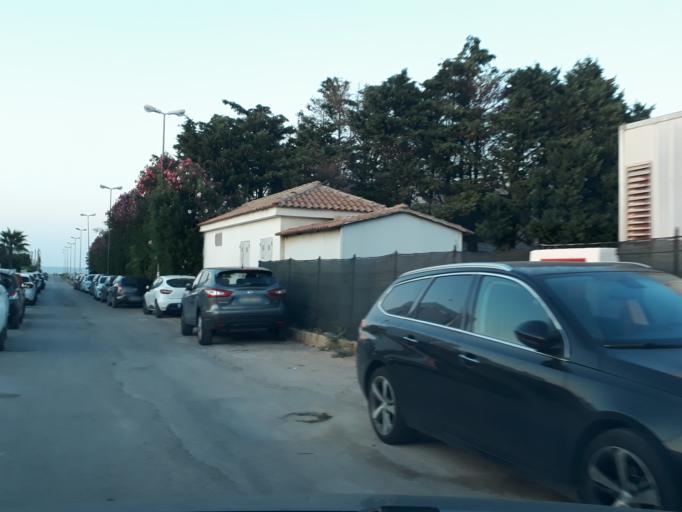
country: IT
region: Apulia
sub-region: Provincia di Brindisi
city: Carovigno
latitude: 40.7531
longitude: 17.7098
